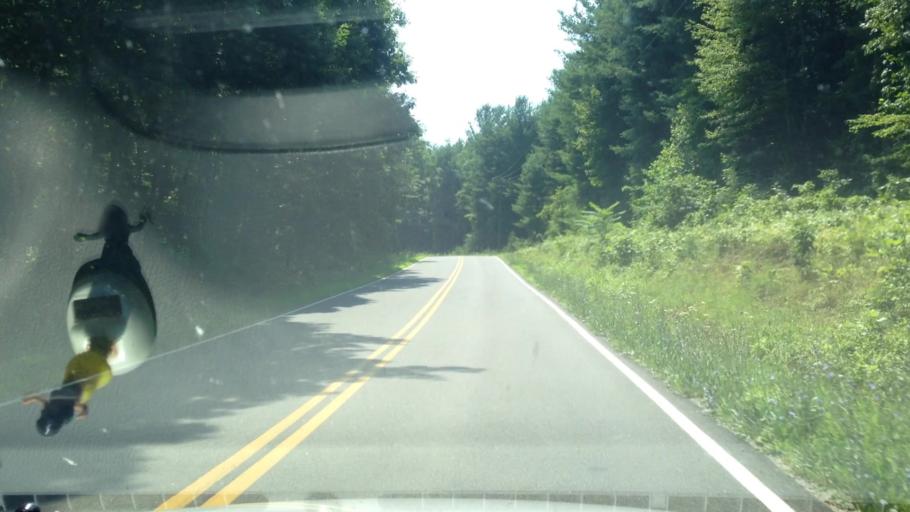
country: US
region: Virginia
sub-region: Patrick County
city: Patrick Springs
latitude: 36.6032
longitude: -80.1683
